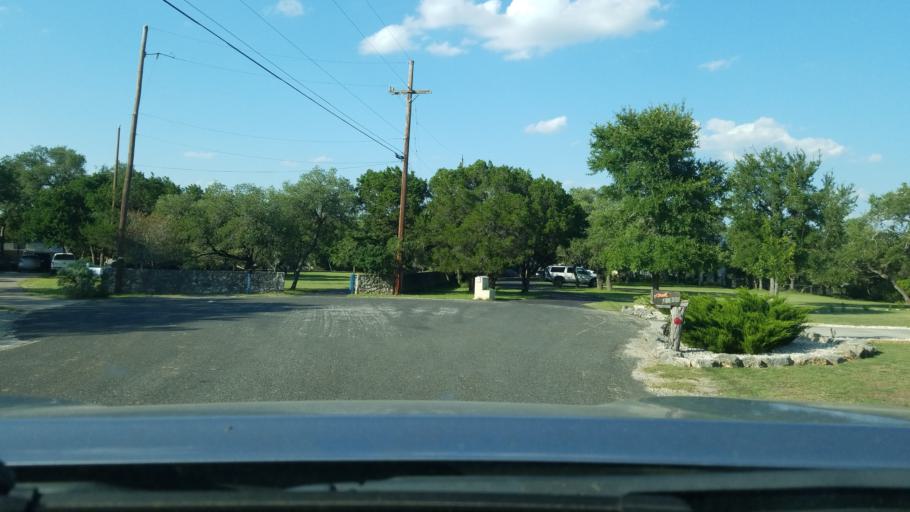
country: US
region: Texas
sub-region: Comal County
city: Bulverde
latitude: 29.7154
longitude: -98.4427
